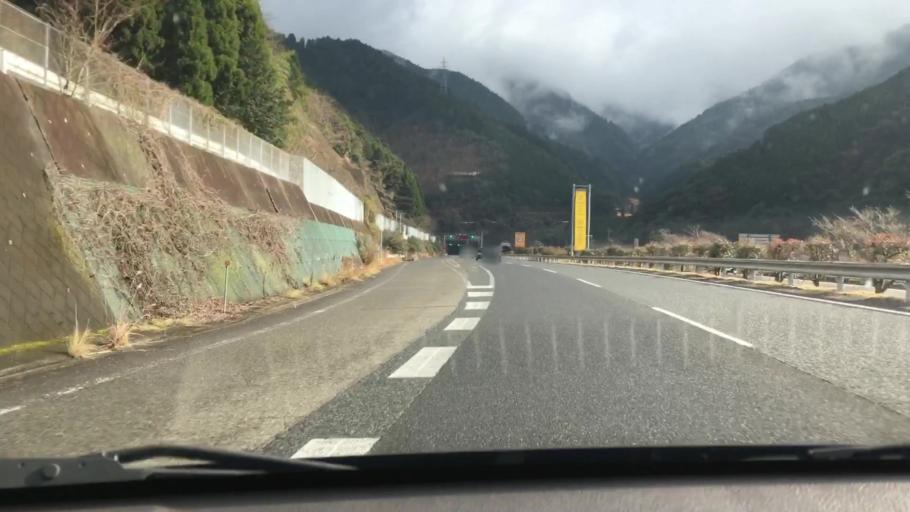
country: JP
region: Kumamoto
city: Yatsushiro
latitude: 32.3976
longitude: 130.7032
